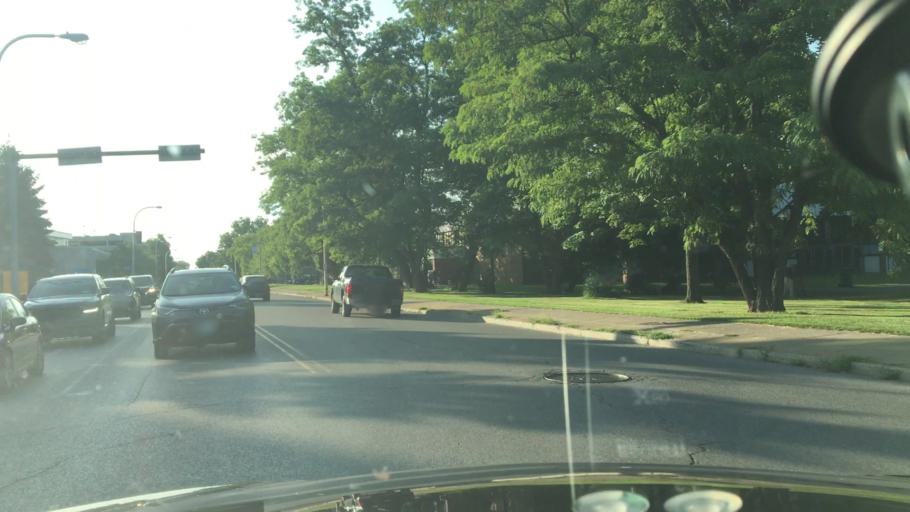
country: US
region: New York
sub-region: Erie County
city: West Seneca
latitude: 42.8466
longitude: -78.8102
